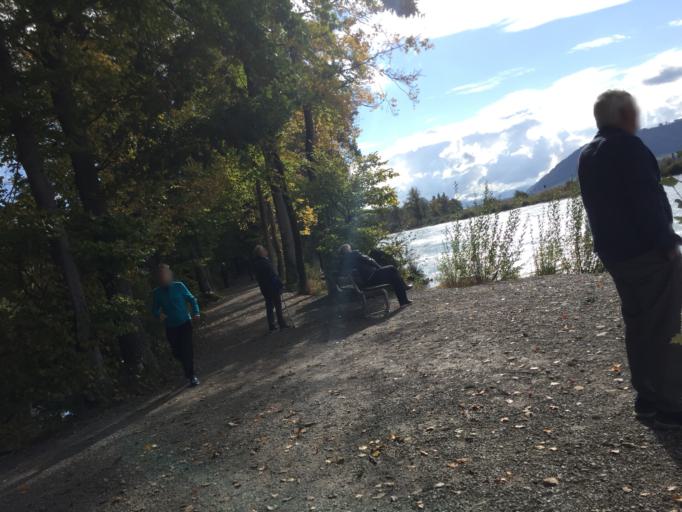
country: CH
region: Bern
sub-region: Bern-Mittelland District
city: Muri
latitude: 46.9251
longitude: 7.4873
